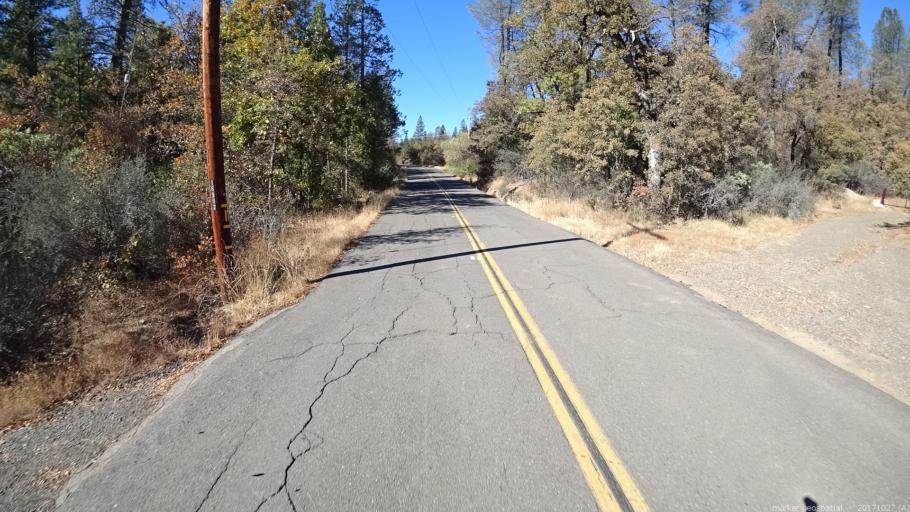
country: US
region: California
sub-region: Shasta County
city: Shingletown
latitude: 40.7519
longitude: -121.9514
